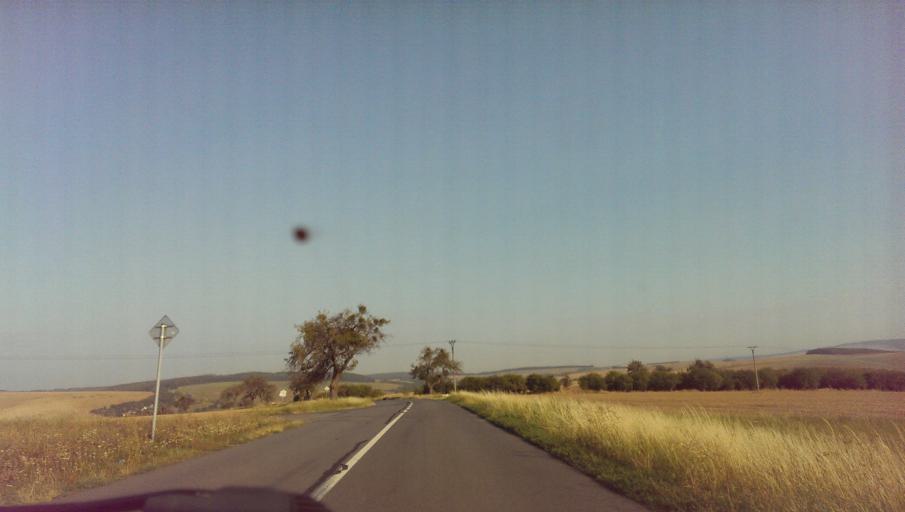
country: CZ
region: Zlin
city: Korycany
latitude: 49.1078
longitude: 17.1528
